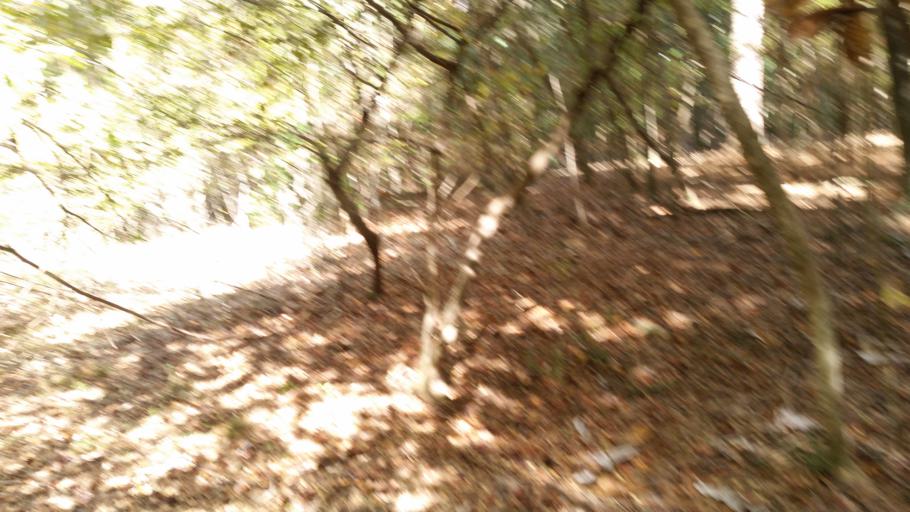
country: US
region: Alabama
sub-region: Baldwin County
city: Spanish Fort
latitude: 30.7382
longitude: -87.9243
